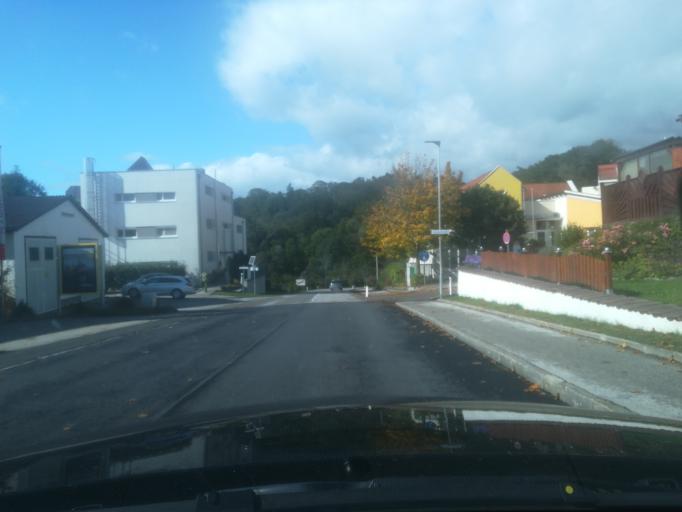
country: AT
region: Upper Austria
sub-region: Politischer Bezirk Urfahr-Umgebung
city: Eidenberg
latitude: 48.3606
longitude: 14.2571
